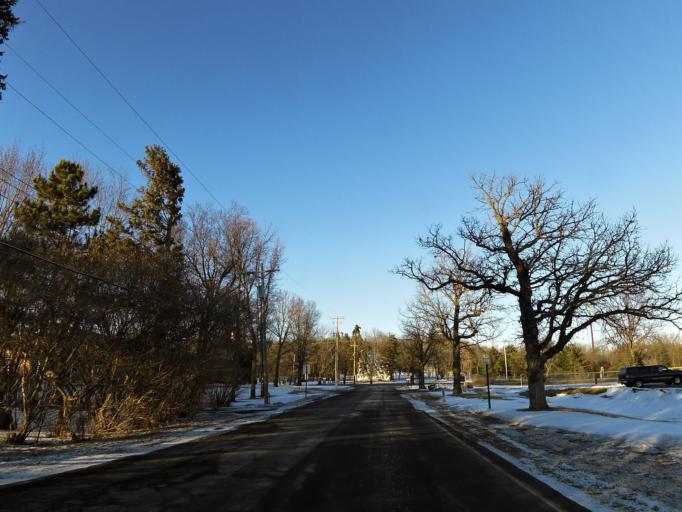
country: US
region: Minnesota
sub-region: Washington County
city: Cottage Grove
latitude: 44.8469
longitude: -92.8807
